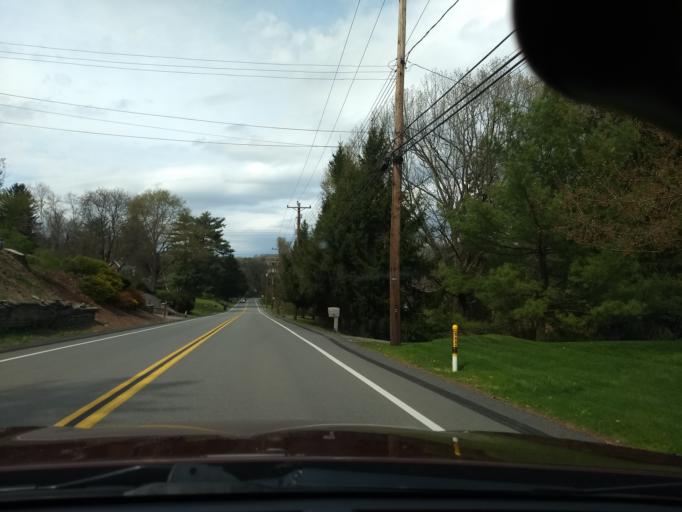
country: US
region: Pennsylvania
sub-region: Allegheny County
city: Allison Park
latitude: 40.5682
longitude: -79.9974
